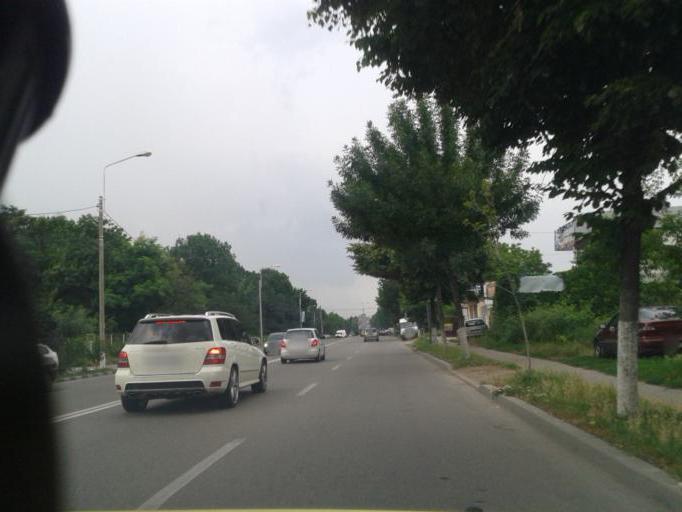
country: RO
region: Prahova
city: Ploiesti
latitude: 44.9541
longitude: 26.0469
